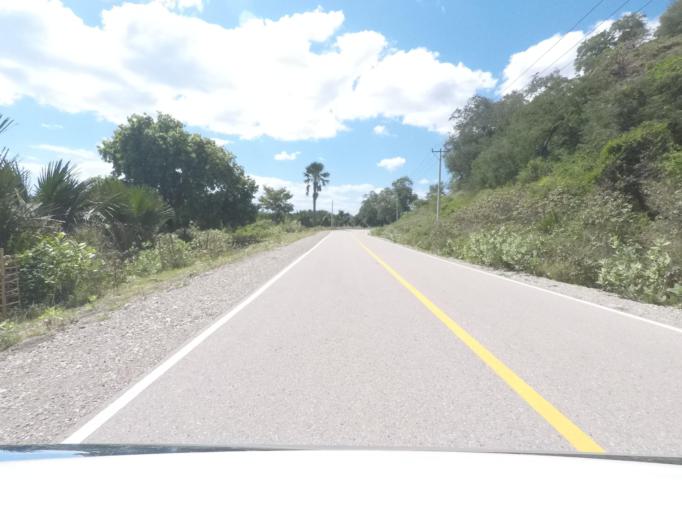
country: TL
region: Lautem
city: Lospalos
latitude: -8.4154
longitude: 126.7994
